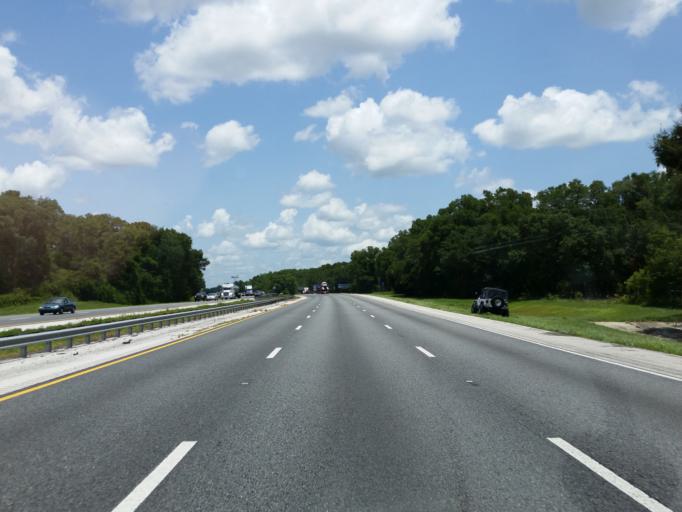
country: US
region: Florida
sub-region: Marion County
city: Ocala
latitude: 29.2547
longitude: -82.1896
